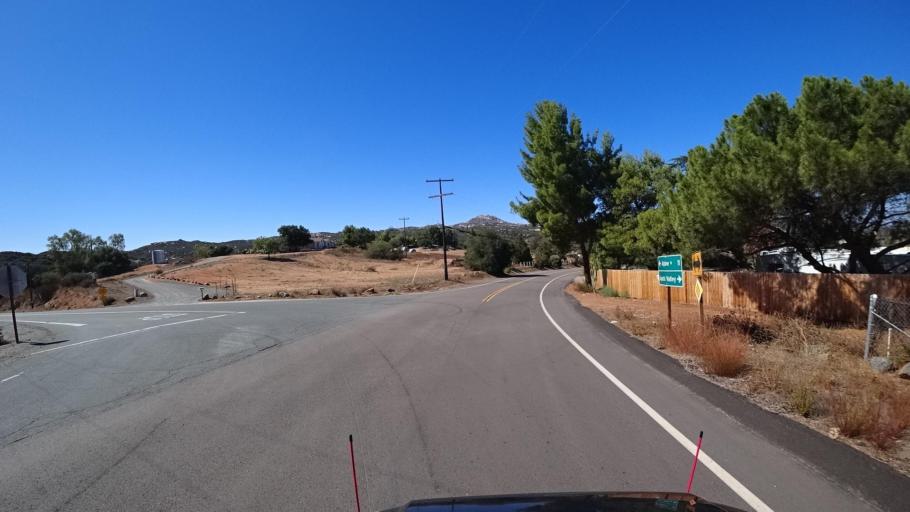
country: US
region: California
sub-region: San Diego County
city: Descanso
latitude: 32.7646
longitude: -116.6752
